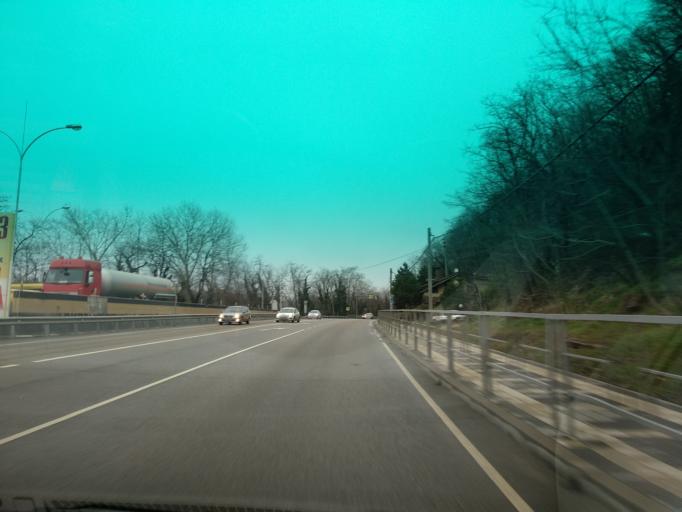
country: RU
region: Krasnodarskiy
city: Tuapse
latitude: 44.1061
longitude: 39.0749
